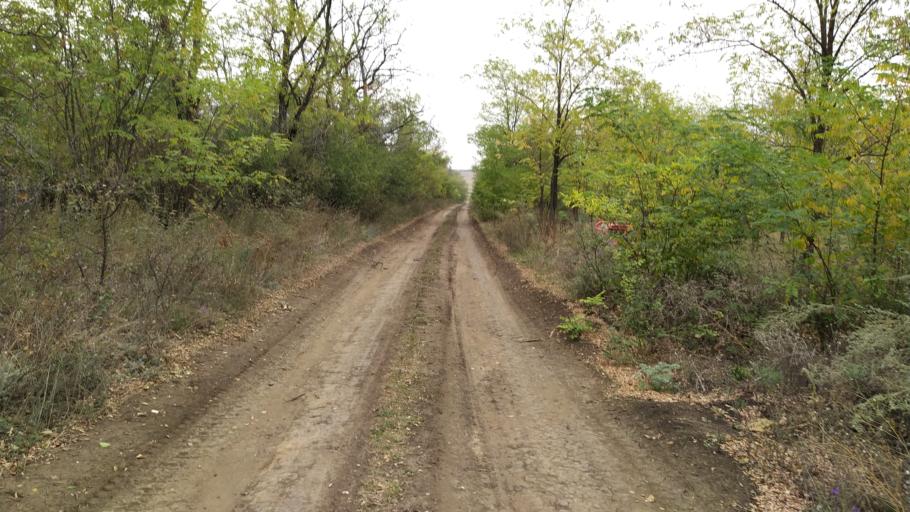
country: RU
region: Rostov
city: Gornyy
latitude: 47.8874
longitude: 40.2399
